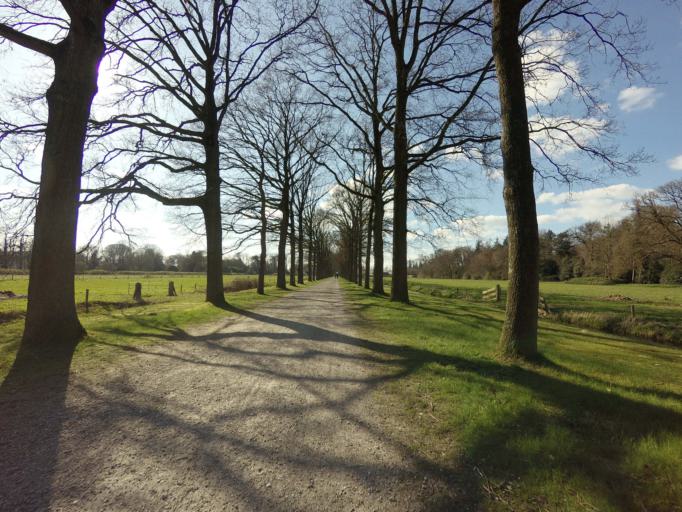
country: NL
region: North Holland
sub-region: Gemeente Wijdemeren
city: Kortenhoef
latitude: 52.2512
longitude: 5.1300
